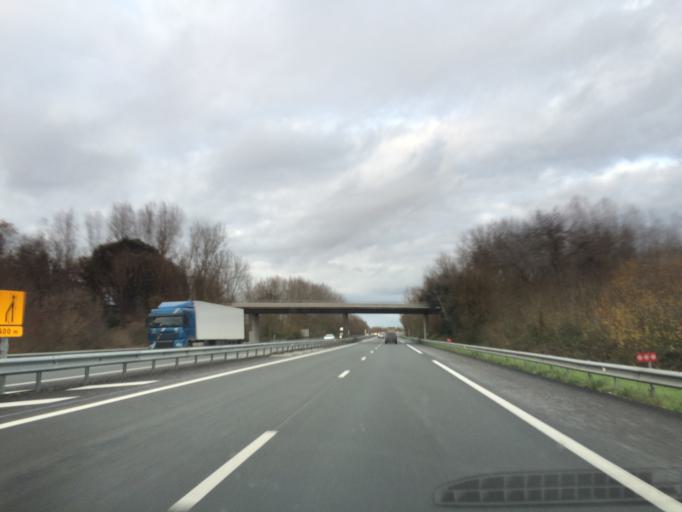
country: FR
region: Poitou-Charentes
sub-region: Departement des Deux-Sevres
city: Fors
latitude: 46.2534
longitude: -0.4230
